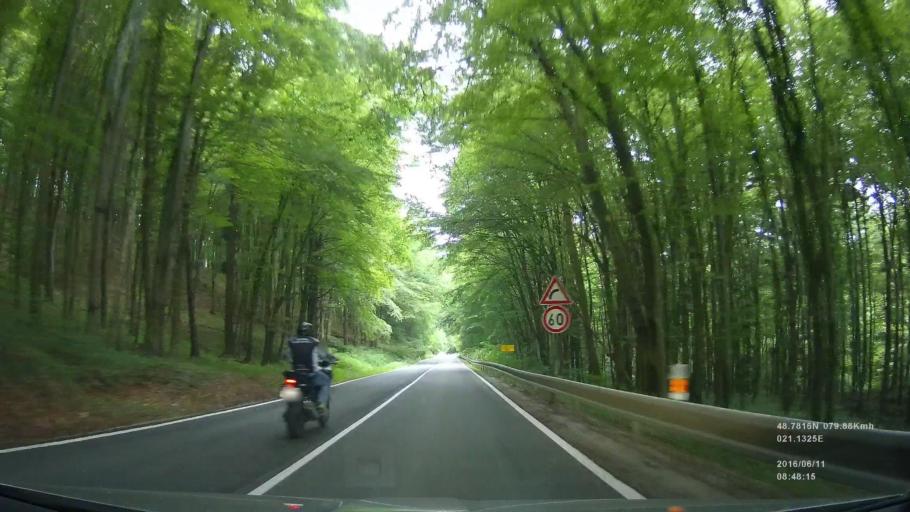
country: SK
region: Kosicky
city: Kosice
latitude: 48.7761
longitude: 21.1370
